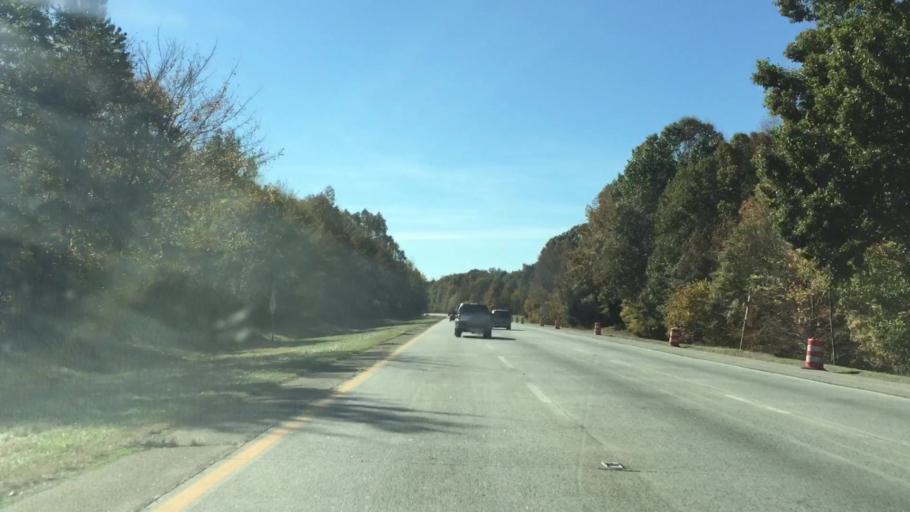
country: US
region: North Carolina
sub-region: Davidson County
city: Thomasville
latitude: 35.8338
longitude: -80.1411
